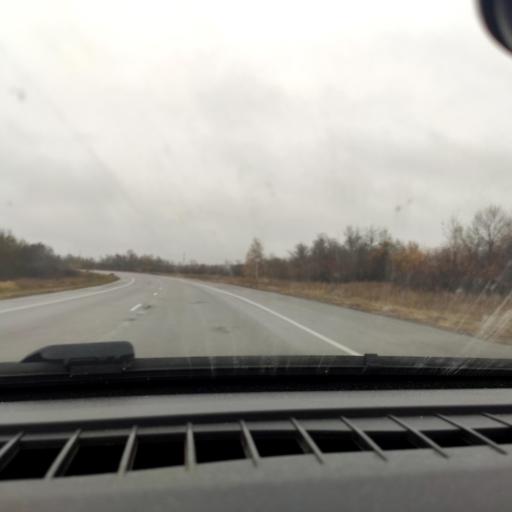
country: RU
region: Voronezj
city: Kolodeznyy
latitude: 51.3042
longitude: 39.0393
